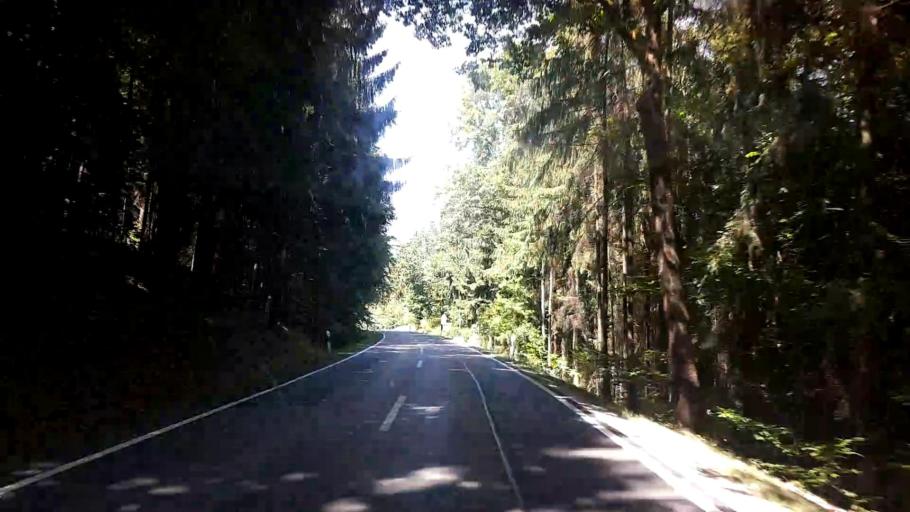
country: DE
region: Bavaria
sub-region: Upper Franconia
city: Weitramsdorf
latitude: 50.2326
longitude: 10.9002
